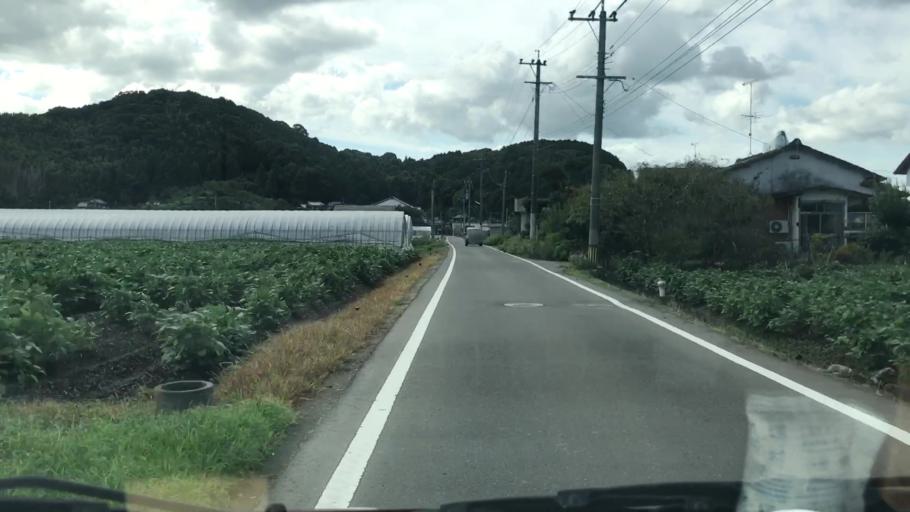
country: JP
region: Saga Prefecture
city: Kashima
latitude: 33.1166
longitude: 130.0741
